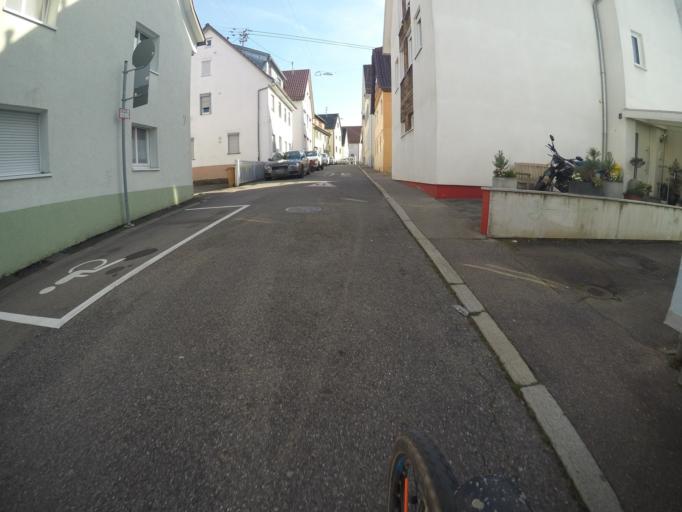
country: DE
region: Baden-Wuerttemberg
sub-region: Regierungsbezirk Stuttgart
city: Fellbach
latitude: 48.8058
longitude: 9.2775
